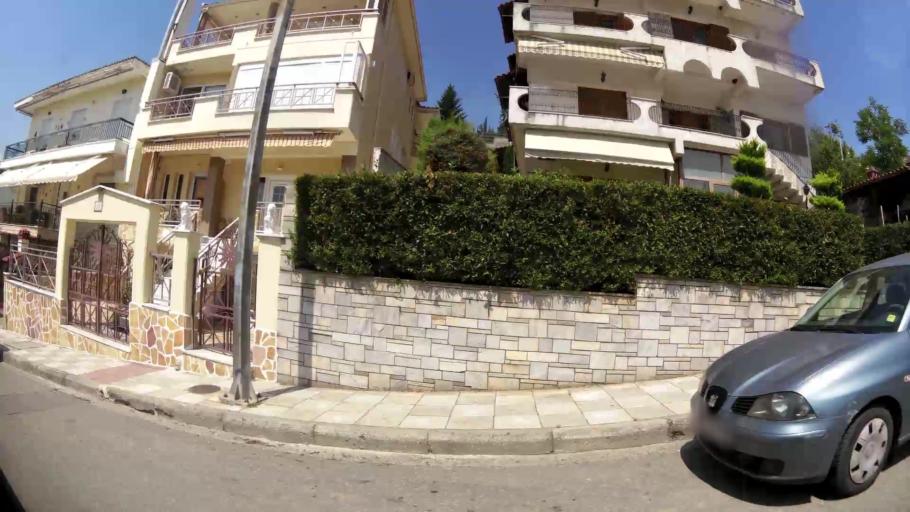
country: GR
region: West Macedonia
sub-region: Nomos Kozanis
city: Kozani
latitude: 40.3089
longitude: 21.7842
